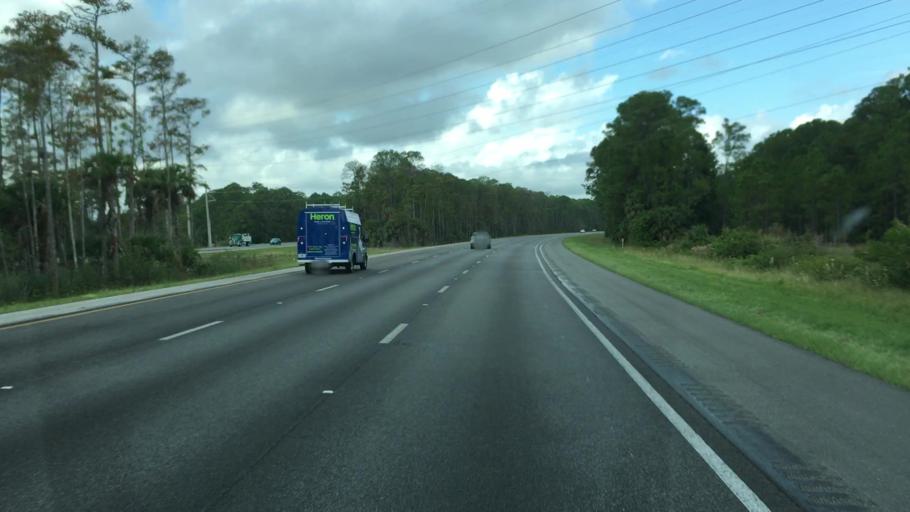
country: US
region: Florida
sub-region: Volusia County
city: Port Orange
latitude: 29.1280
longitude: -81.0567
